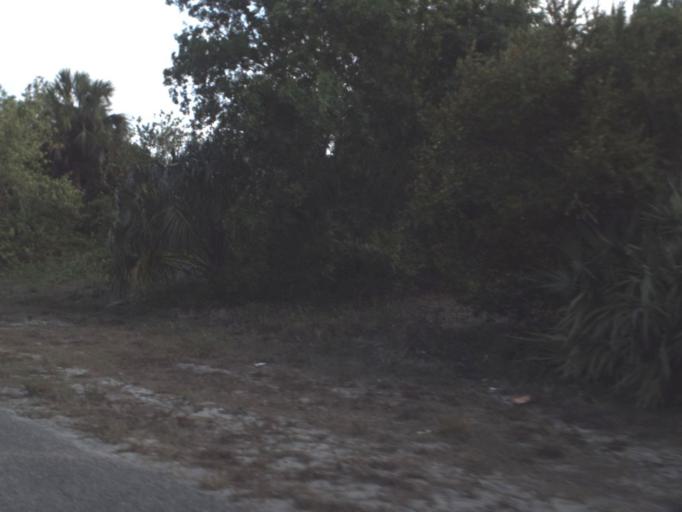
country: US
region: Florida
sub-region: Brevard County
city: Rockledge
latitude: 28.3104
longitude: -80.7085
